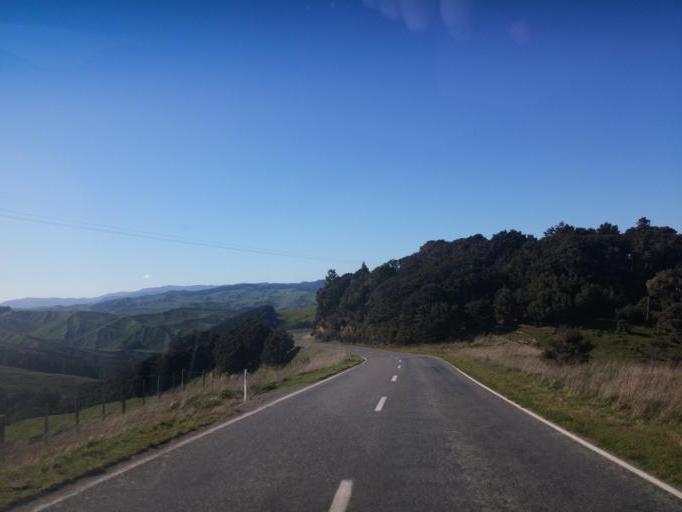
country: NZ
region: Wellington
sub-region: South Wairarapa District
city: Waipawa
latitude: -41.3598
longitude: 175.4935
